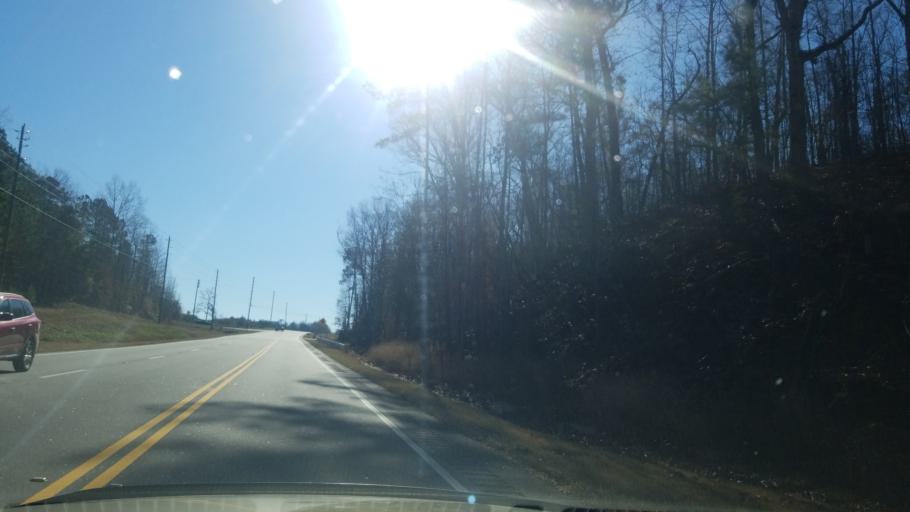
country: US
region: Georgia
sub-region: Troup County
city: West Point
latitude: 32.8589
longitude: -85.1334
